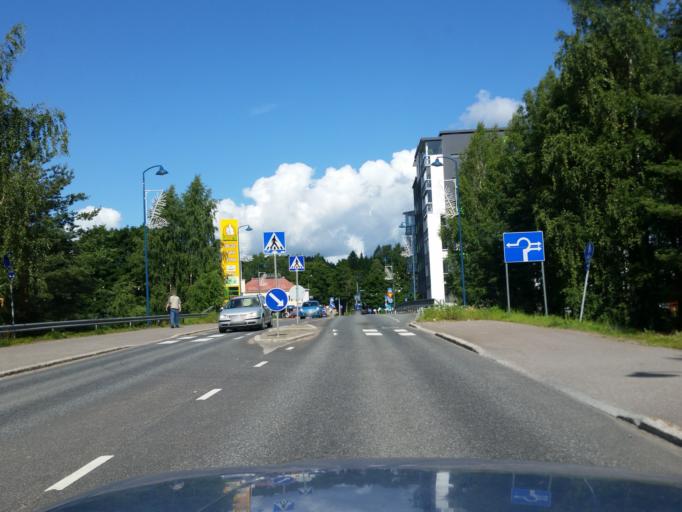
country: FI
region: Uusimaa
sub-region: Helsinki
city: Vihti
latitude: 60.3333
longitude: 24.3225
